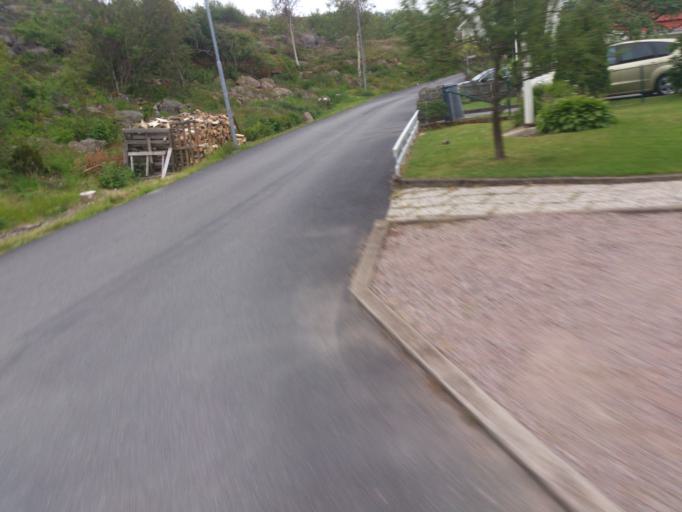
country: SE
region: Vaestra Goetaland
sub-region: Sotenas Kommun
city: Kungshamn
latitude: 58.3809
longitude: 11.2696
